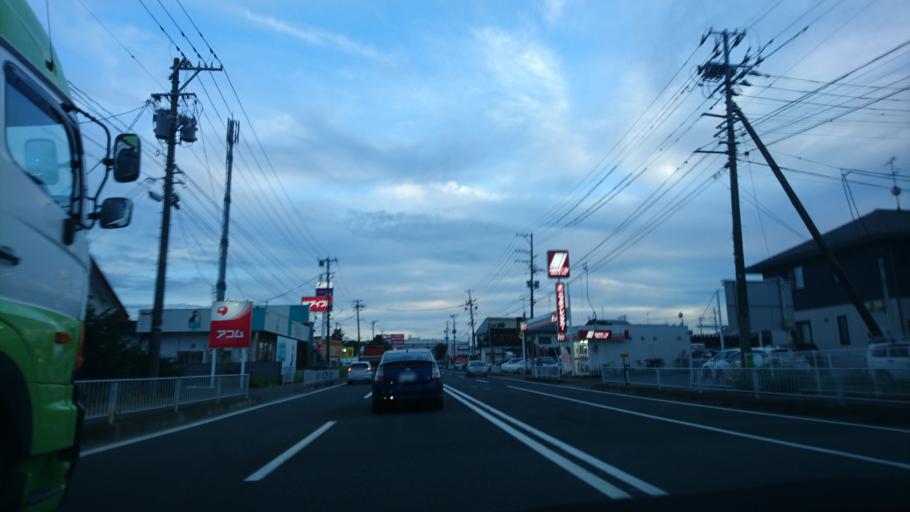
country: JP
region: Iwate
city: Morioka-shi
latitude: 39.6750
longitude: 141.1556
